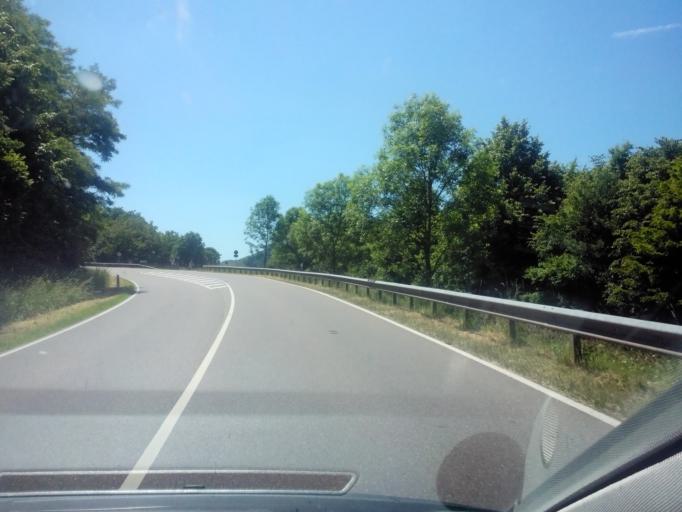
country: DE
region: Rheinland-Pfalz
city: Ockfen
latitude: 49.6203
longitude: 6.5654
